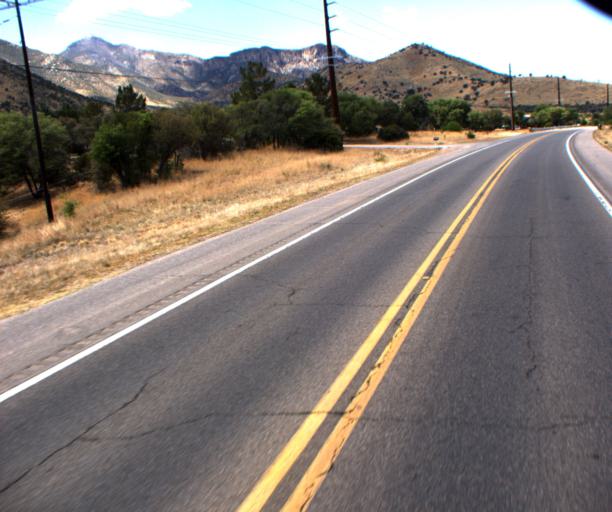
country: US
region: Arizona
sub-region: Cochise County
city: Sierra Vista Southeast
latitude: 31.3977
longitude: -110.2389
